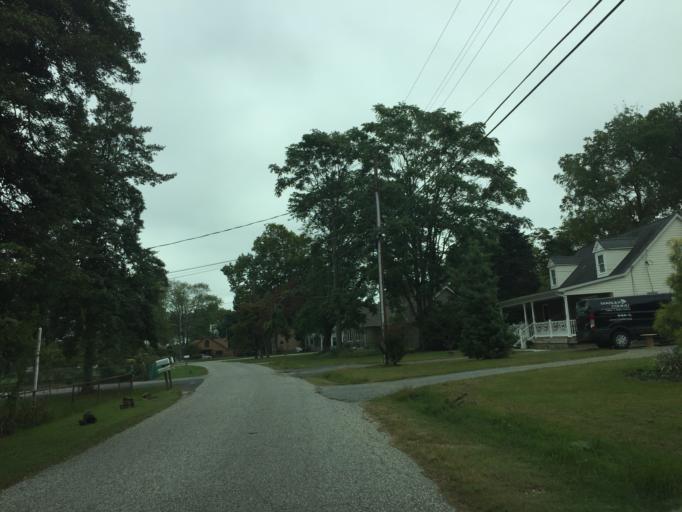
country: US
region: Maryland
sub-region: Baltimore County
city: Bowleys Quarters
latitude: 39.3755
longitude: -76.3871
